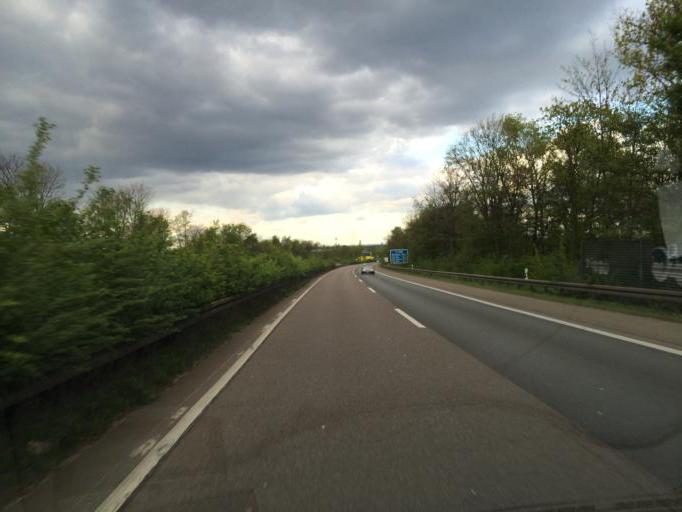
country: DE
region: North Rhine-Westphalia
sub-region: Regierungsbezirk Koln
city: Frechen
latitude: 50.8950
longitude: 6.8278
